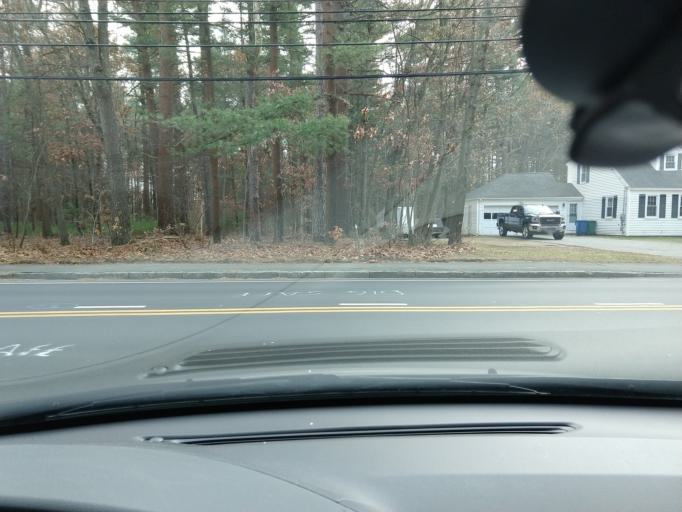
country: US
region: Massachusetts
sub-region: Middlesex County
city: Billerica
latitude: 42.5848
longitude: -71.2989
